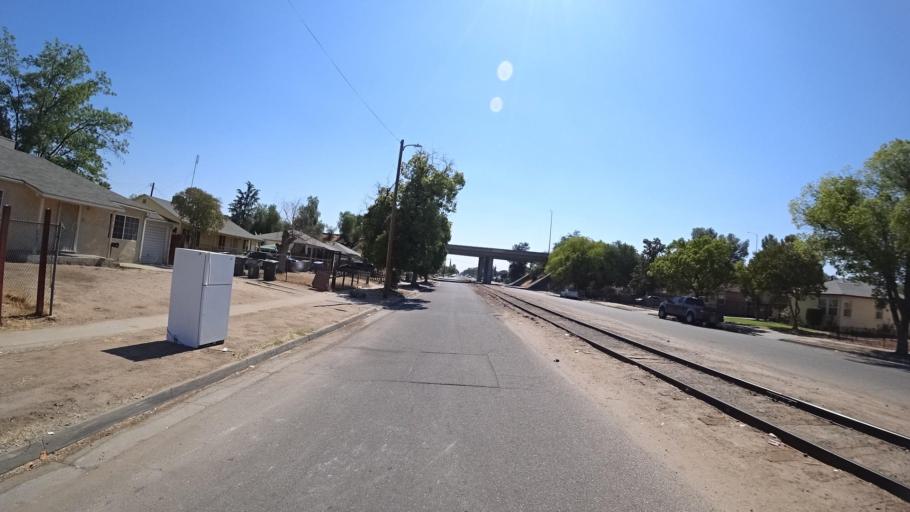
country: US
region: California
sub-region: Fresno County
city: Fresno
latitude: 36.7614
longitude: -119.7768
